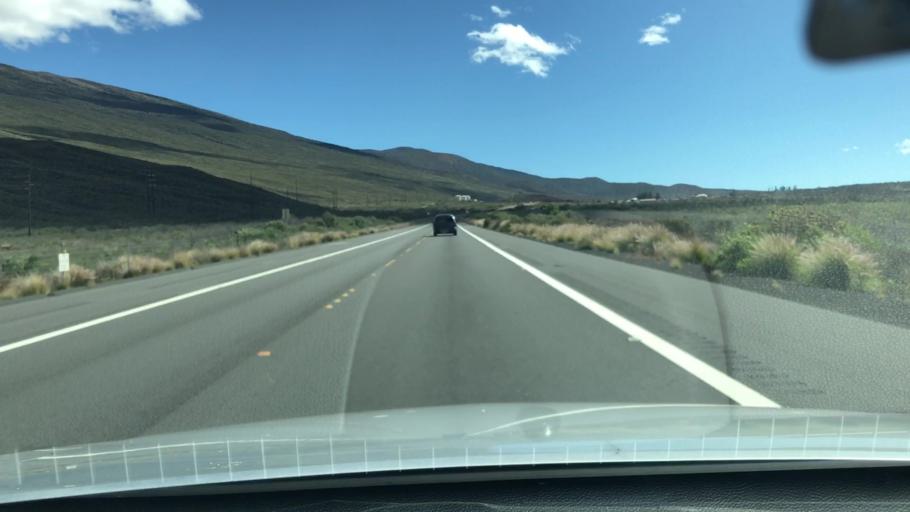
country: US
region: Hawaii
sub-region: Hawaii County
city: Waimea
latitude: 19.7639
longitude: -155.5562
